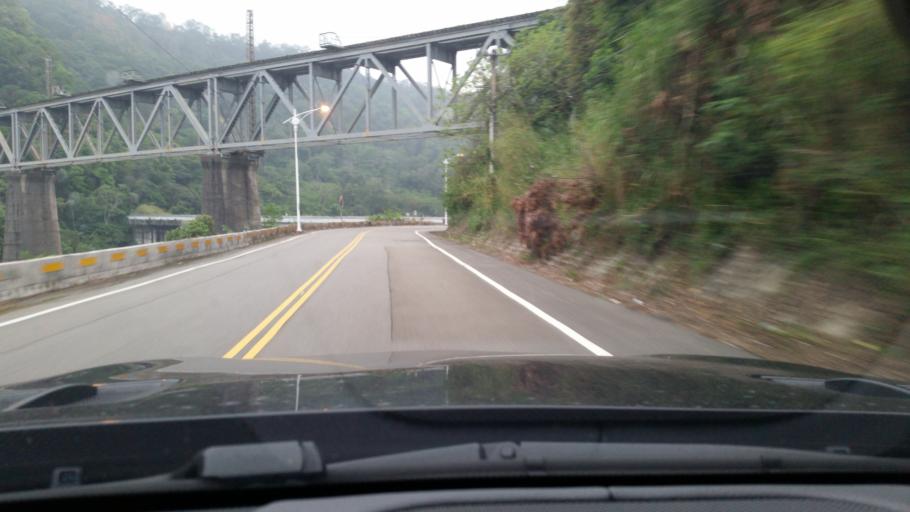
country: TW
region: Taiwan
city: Fengyuan
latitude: 24.3412
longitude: 120.7672
